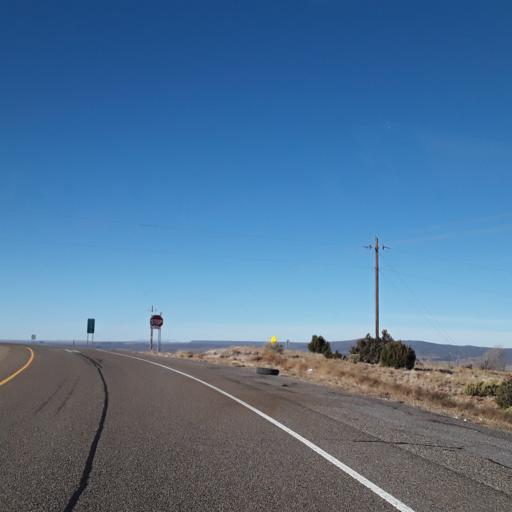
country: US
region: New Mexico
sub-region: Sandoval County
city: Santo Domingo Pueblo
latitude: 35.4604
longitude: -106.3300
